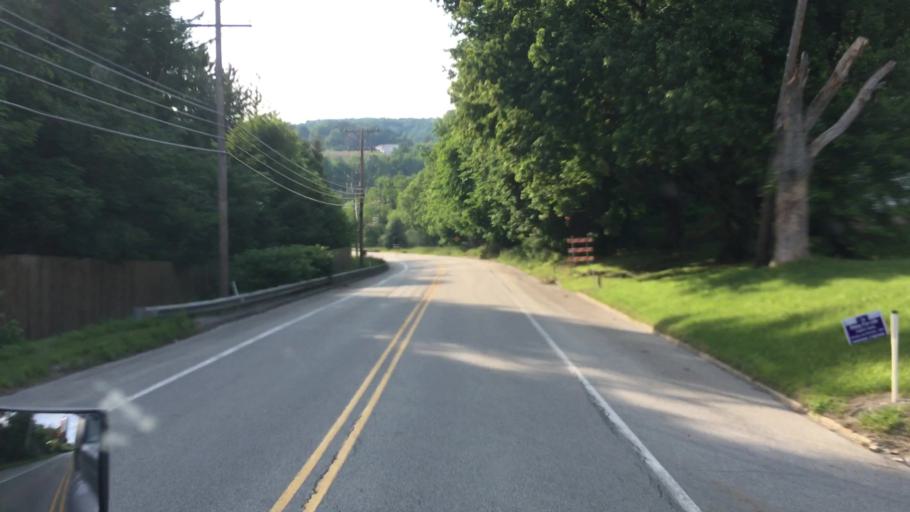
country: US
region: Pennsylvania
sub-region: Fayette County
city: Hopwood
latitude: 39.8043
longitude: -79.5570
